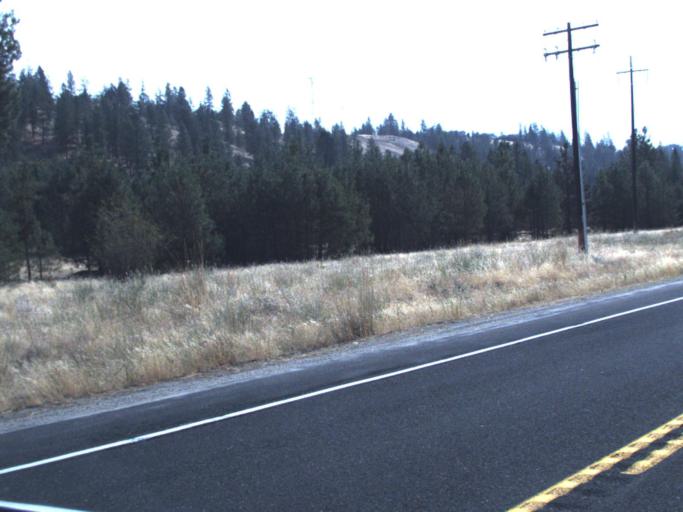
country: US
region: Washington
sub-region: Spokane County
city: Town and Country
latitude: 47.7567
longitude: -117.5182
